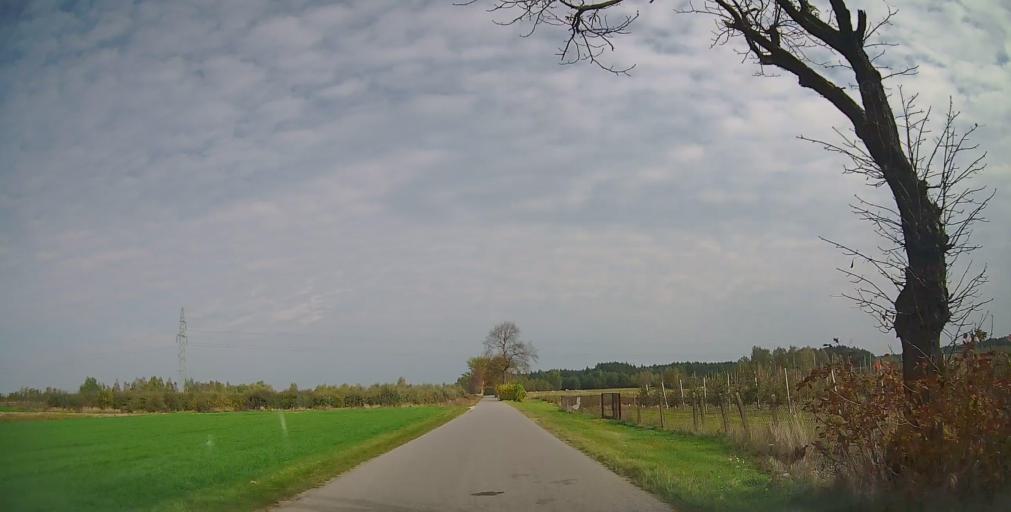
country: PL
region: Masovian Voivodeship
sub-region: Powiat bialobrzeski
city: Wysmierzyce
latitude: 51.6486
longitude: 20.7623
